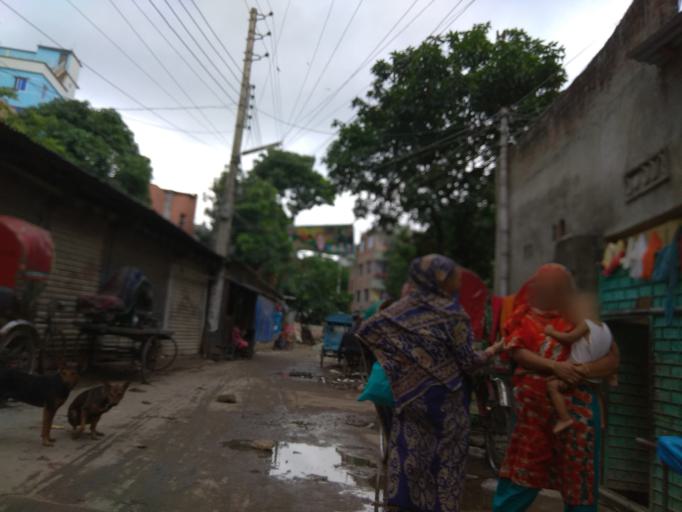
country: BD
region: Dhaka
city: Azimpur
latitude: 23.7926
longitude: 90.3845
